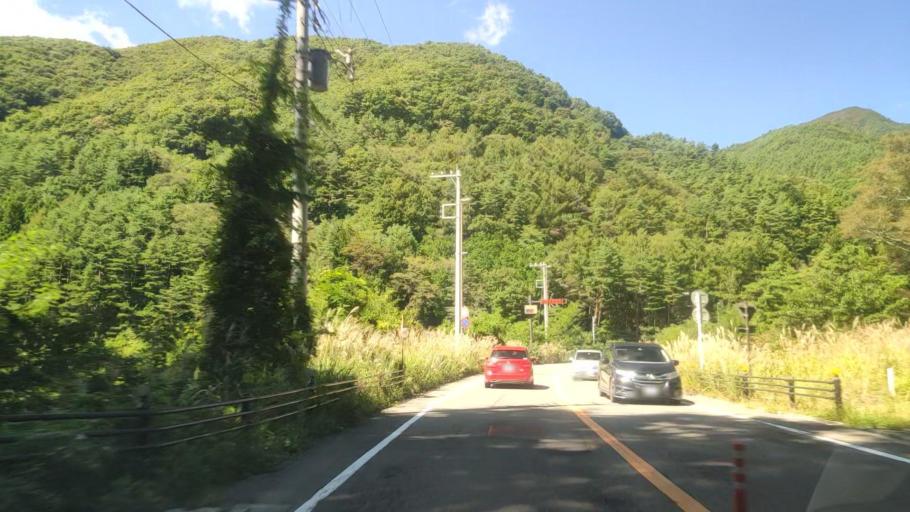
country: JP
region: Yamanashi
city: Fujikawaguchiko
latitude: 35.5386
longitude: 138.7723
